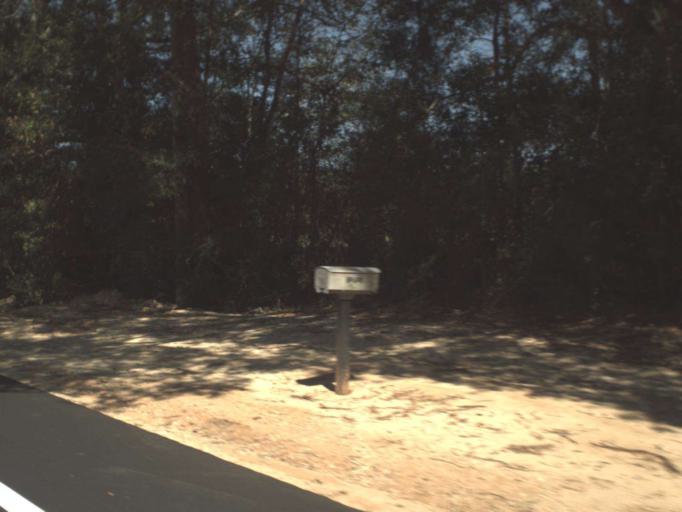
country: US
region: Alabama
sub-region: Covington County
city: Florala
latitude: 30.8611
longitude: -86.2507
